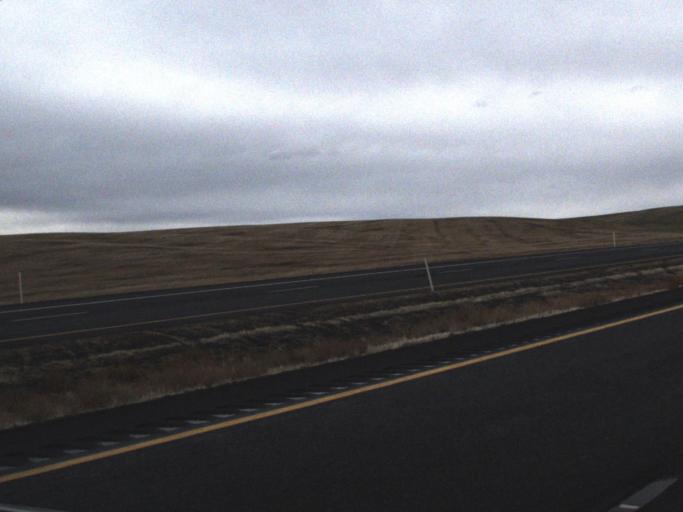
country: US
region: Washington
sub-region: Walla Walla County
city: Garrett
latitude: 46.0542
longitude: -118.4656
